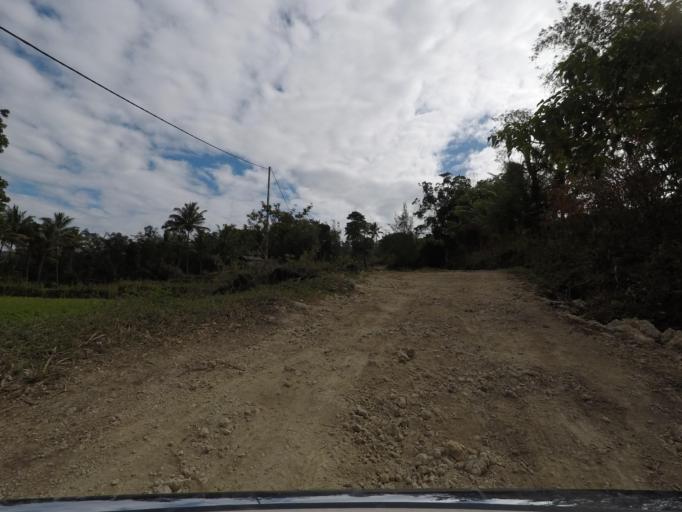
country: TL
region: Baucau
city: Venilale
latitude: -8.6491
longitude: 126.3925
